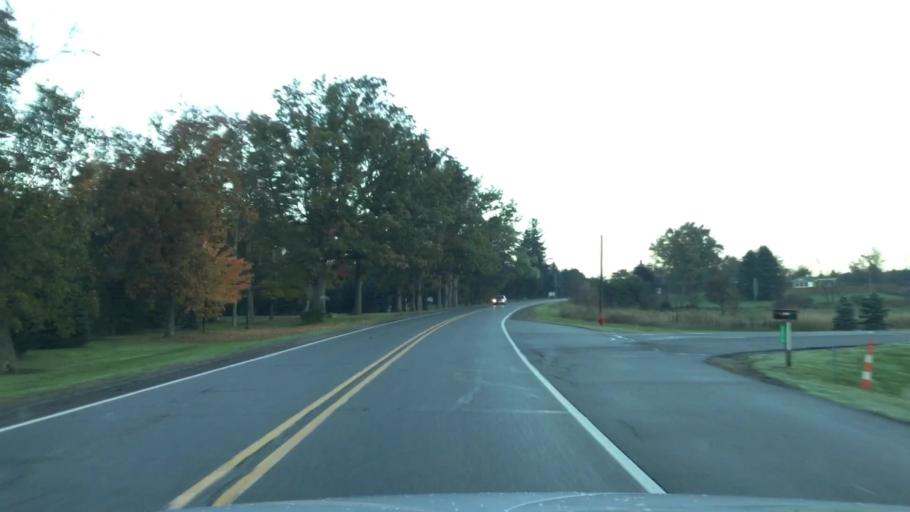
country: US
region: Michigan
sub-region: Livingston County
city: Howell
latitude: 42.6423
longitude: -83.9347
